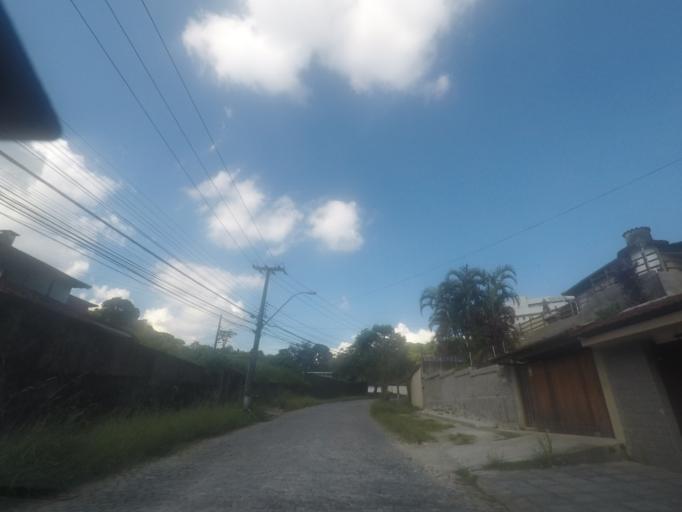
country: BR
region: Rio de Janeiro
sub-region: Petropolis
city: Petropolis
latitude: -22.5217
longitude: -43.2064
